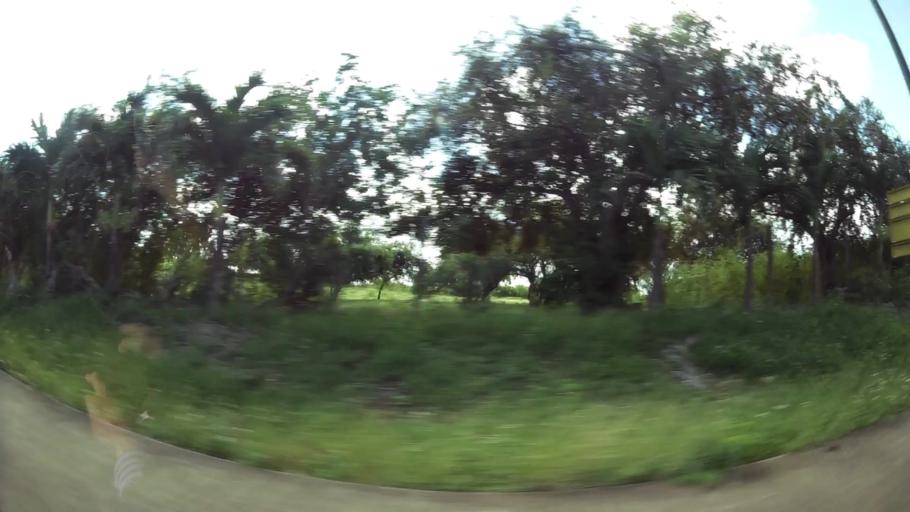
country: GP
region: Guadeloupe
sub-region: Guadeloupe
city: Anse-Bertrand
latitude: 16.4650
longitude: -61.4883
